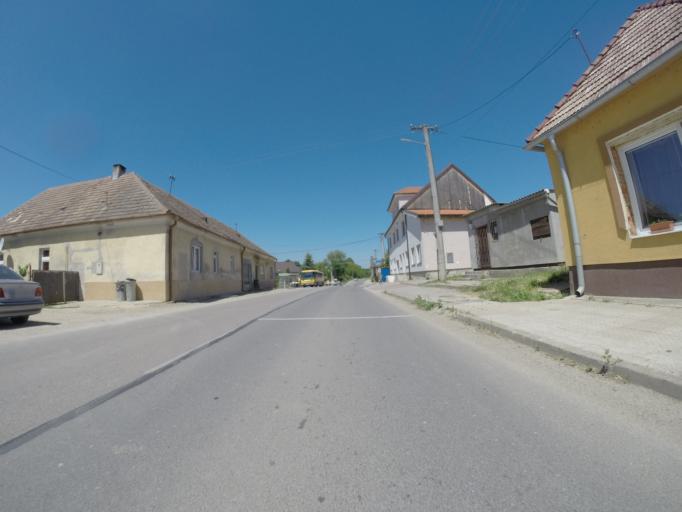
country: SK
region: Trnavsky
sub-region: Okres Trnava
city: Piestany
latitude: 48.5023
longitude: 17.9834
